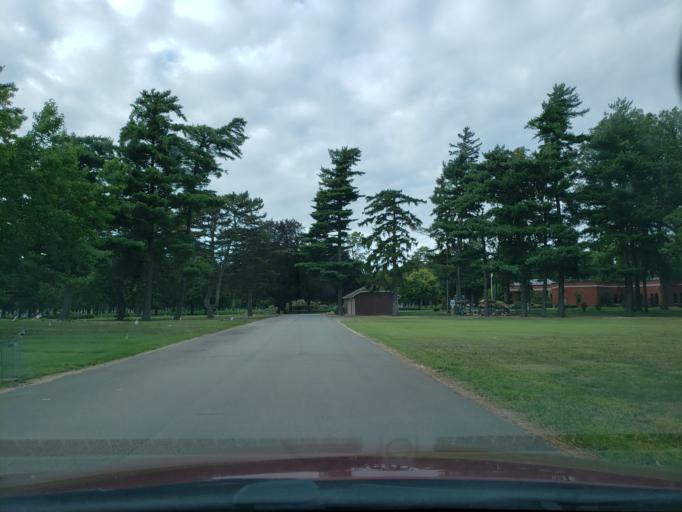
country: US
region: New York
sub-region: Monroe County
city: Irondequoit
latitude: 43.2122
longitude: -77.6312
